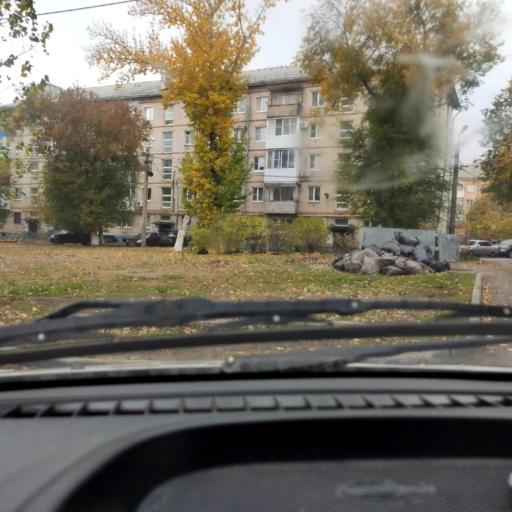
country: RU
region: Samara
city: Zhigulevsk
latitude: 53.4758
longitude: 49.4797
